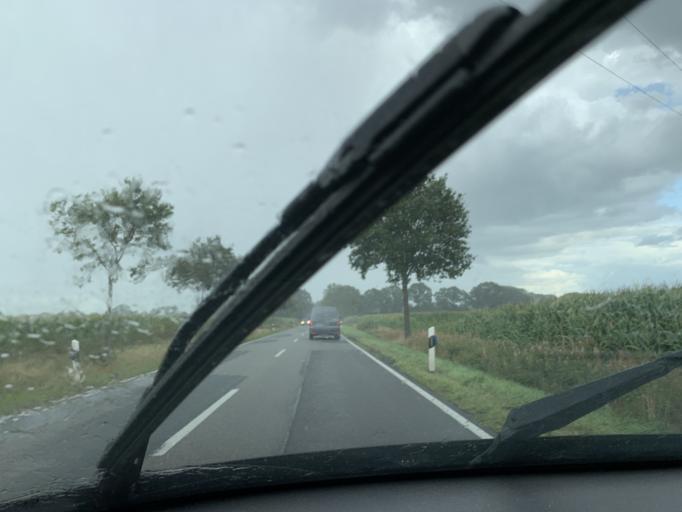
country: DE
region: Lower Saxony
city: Wiefelstede
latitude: 53.2983
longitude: 8.0508
